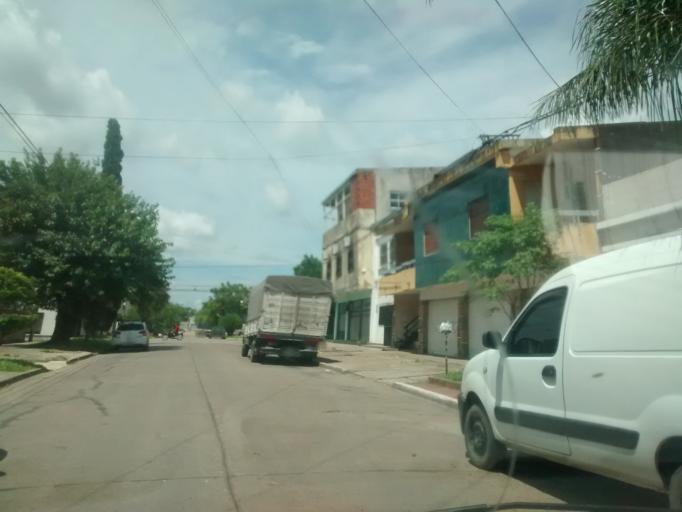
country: AR
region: Chaco
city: Resistencia
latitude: -27.4459
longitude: -58.9966
